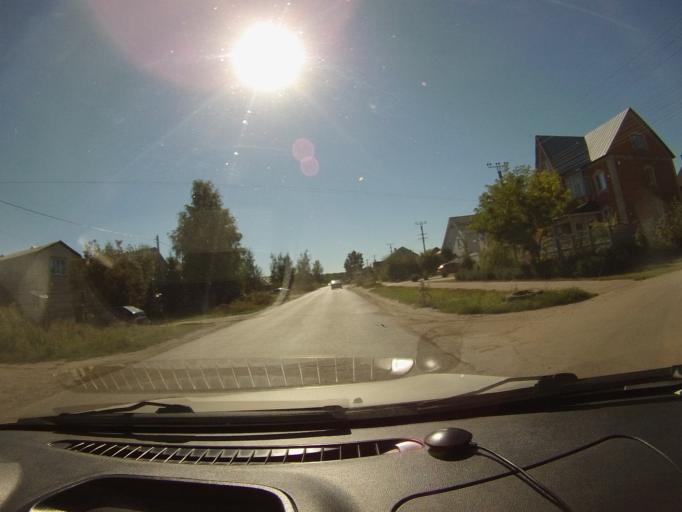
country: RU
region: Tambov
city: Tambov
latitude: 52.7622
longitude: 41.3788
